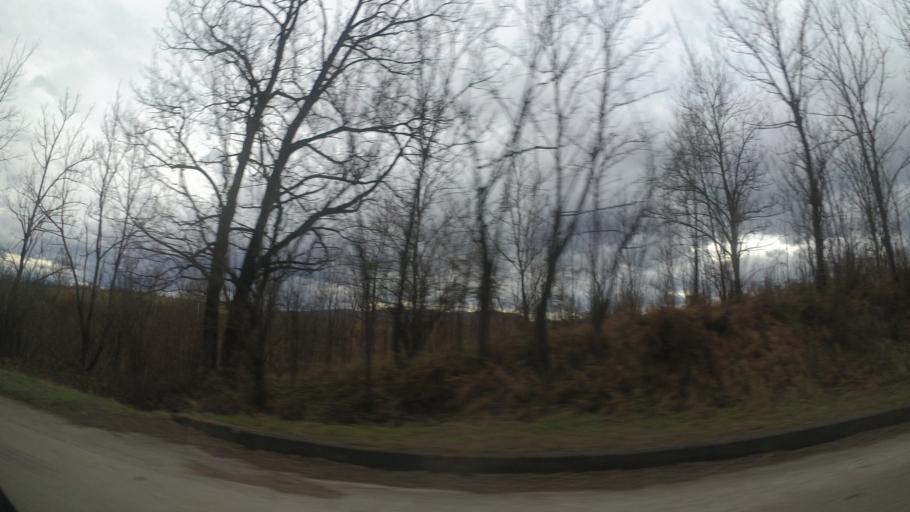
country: HR
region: Karlovacka
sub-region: Grad Karlovac
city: Karlovac
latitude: 45.3652
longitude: 15.5625
